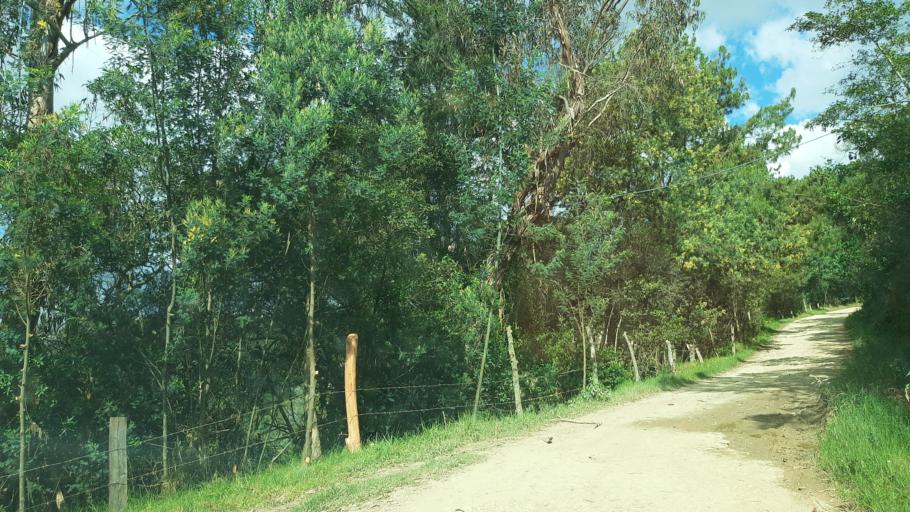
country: CO
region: Boyaca
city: Santa Sofia
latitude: 5.7336
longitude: -73.5545
